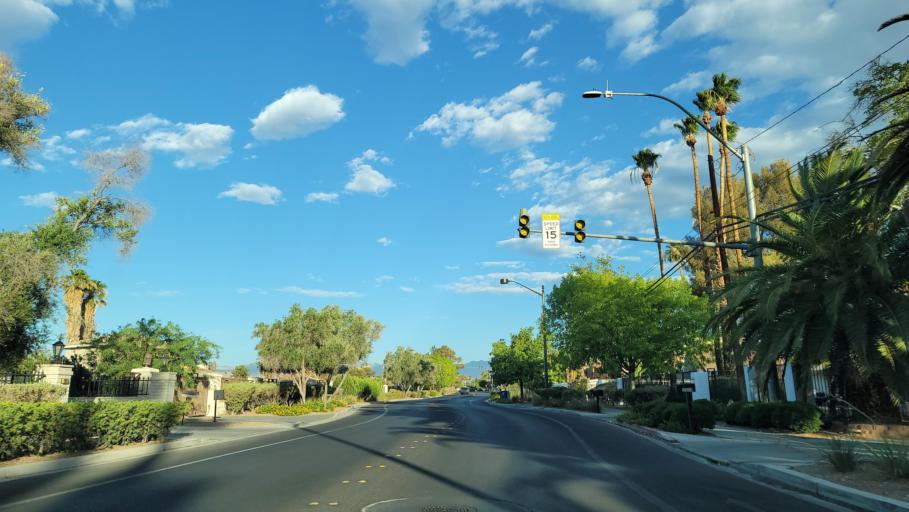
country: US
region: Nevada
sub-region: Clark County
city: Las Vegas
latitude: 36.1662
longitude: -115.1797
